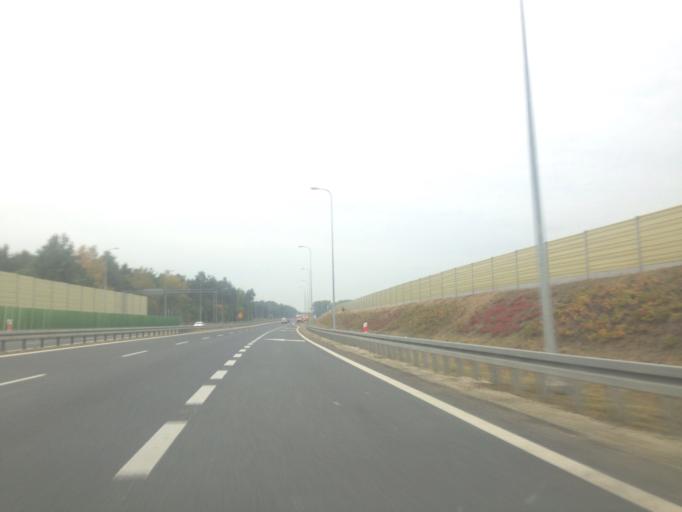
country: PL
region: Greater Poland Voivodeship
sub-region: Powiat gnieznienski
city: Lubowo
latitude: 52.4547
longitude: 17.3836
